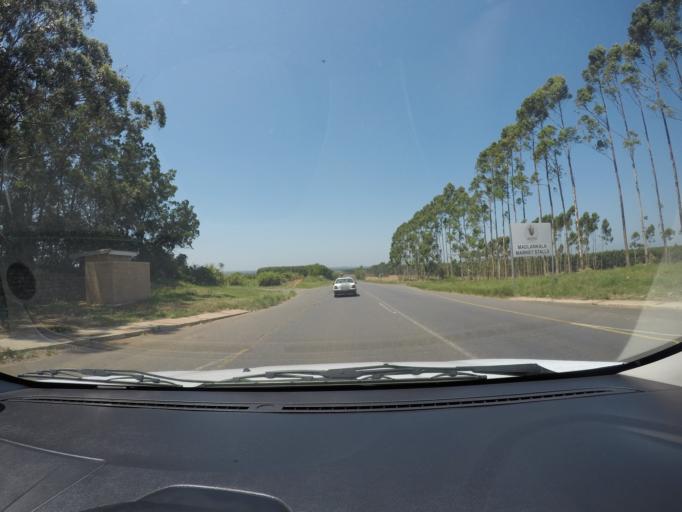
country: ZA
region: KwaZulu-Natal
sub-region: uThungulu District Municipality
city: eSikhawini
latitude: -28.8229
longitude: 31.9477
